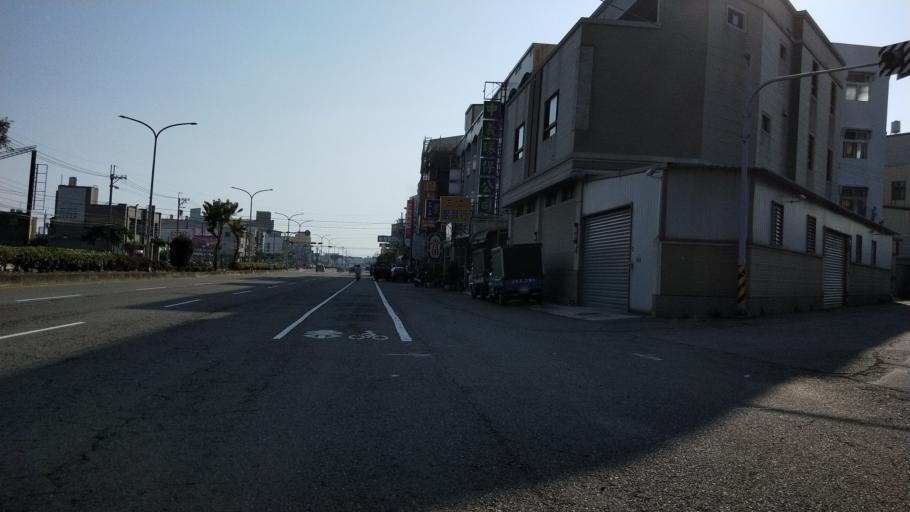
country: TW
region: Taiwan
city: Fengyuan
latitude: 24.2668
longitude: 120.5654
